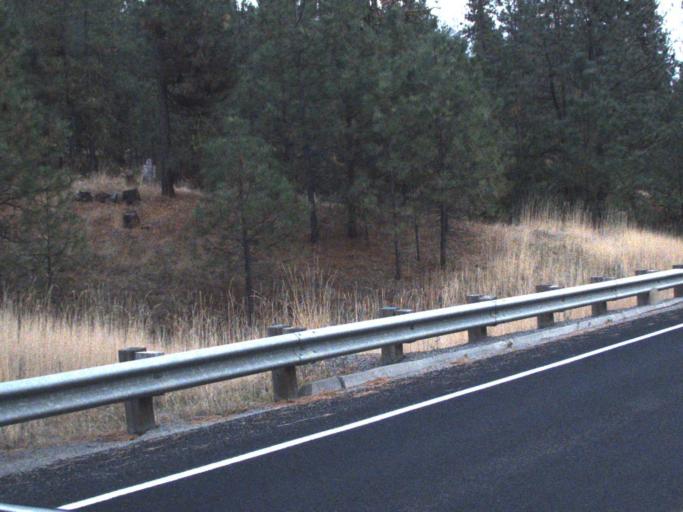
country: US
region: Washington
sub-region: Lincoln County
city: Davenport
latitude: 48.0332
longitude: -118.2308
